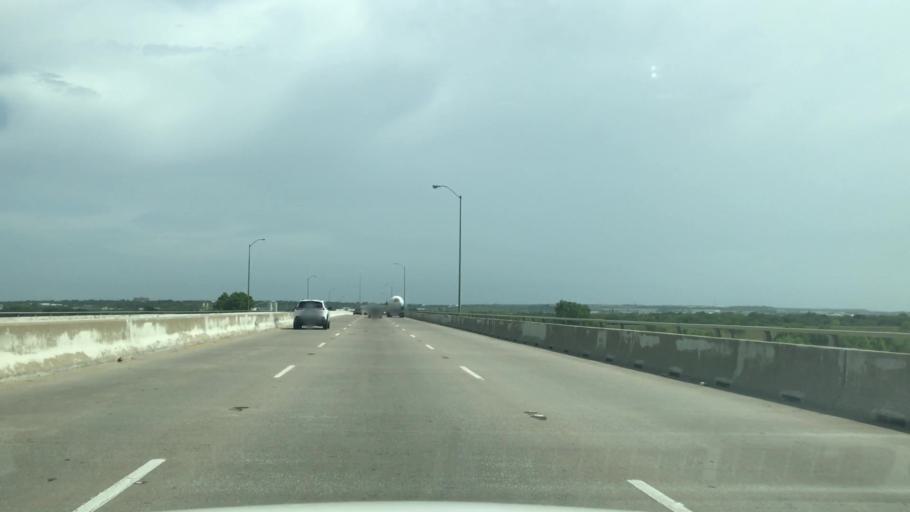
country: US
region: Texas
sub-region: Dallas County
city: Cockrell Hill
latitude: 32.7996
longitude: -96.8739
